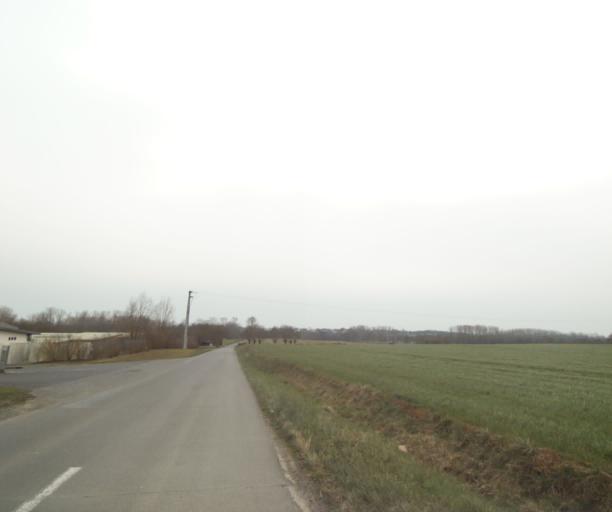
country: FR
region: Poitou-Charentes
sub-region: Departement des Deux-Sevres
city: Bessines
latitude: 46.3123
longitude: -0.5176
